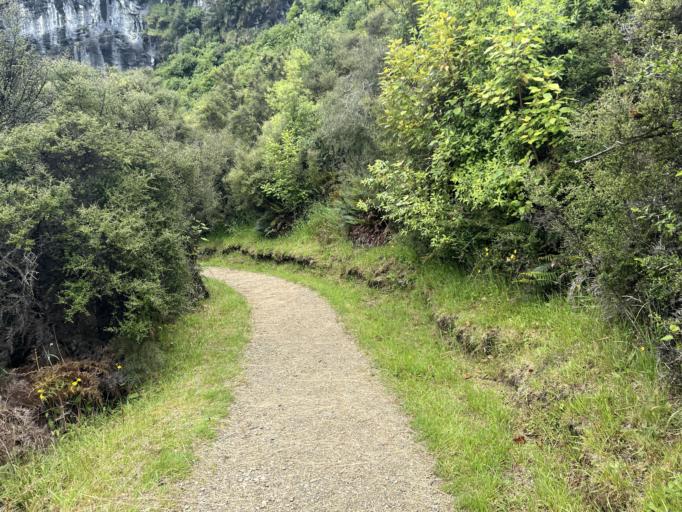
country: NZ
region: Otago
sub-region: Queenstown-Lakes District
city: Wanaka
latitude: -44.6463
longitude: 168.9654
